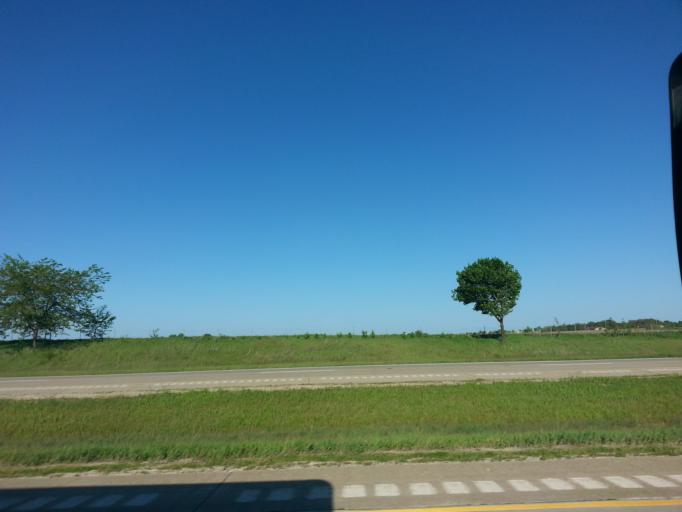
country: US
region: Illinois
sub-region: Woodford County
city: El Paso
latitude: 40.7907
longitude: -89.0356
